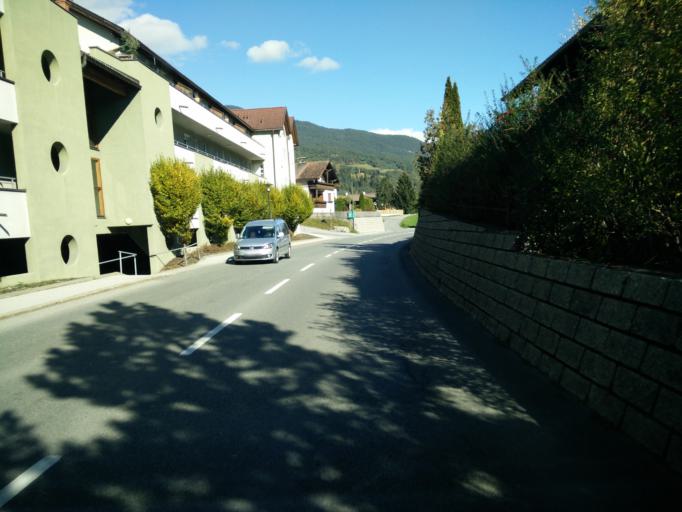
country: AT
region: Tyrol
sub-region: Politischer Bezirk Imst
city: Tarrenz
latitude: 47.2641
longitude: 10.7659
